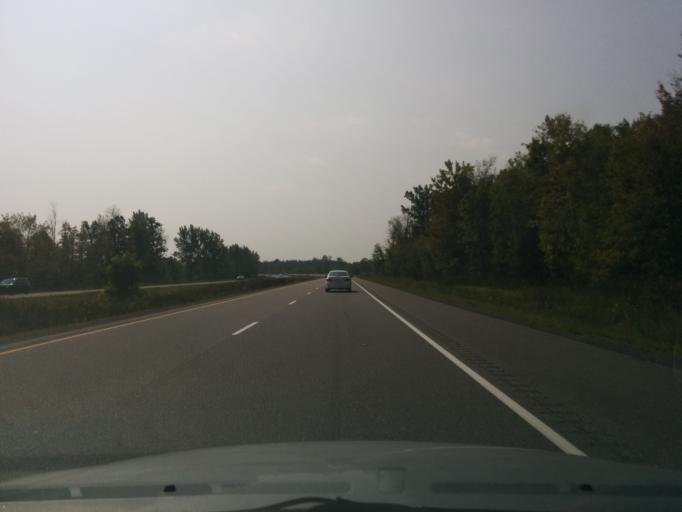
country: CA
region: Ontario
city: Bells Corners
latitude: 45.1239
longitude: -75.6756
